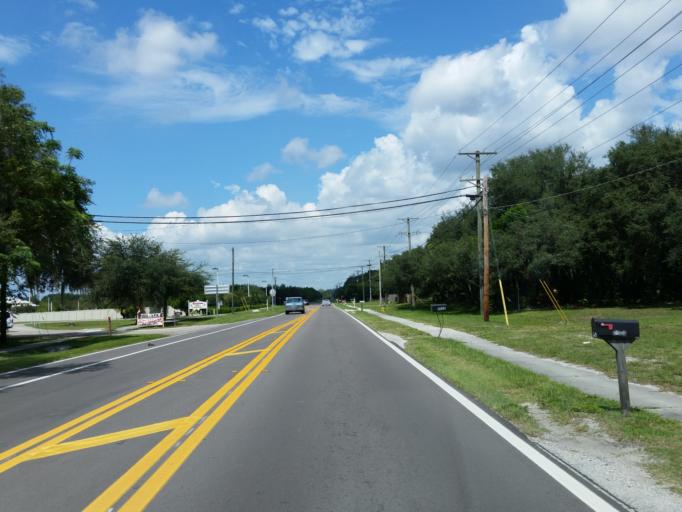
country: US
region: Florida
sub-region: Hillsborough County
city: Riverview
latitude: 27.8309
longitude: -82.3047
